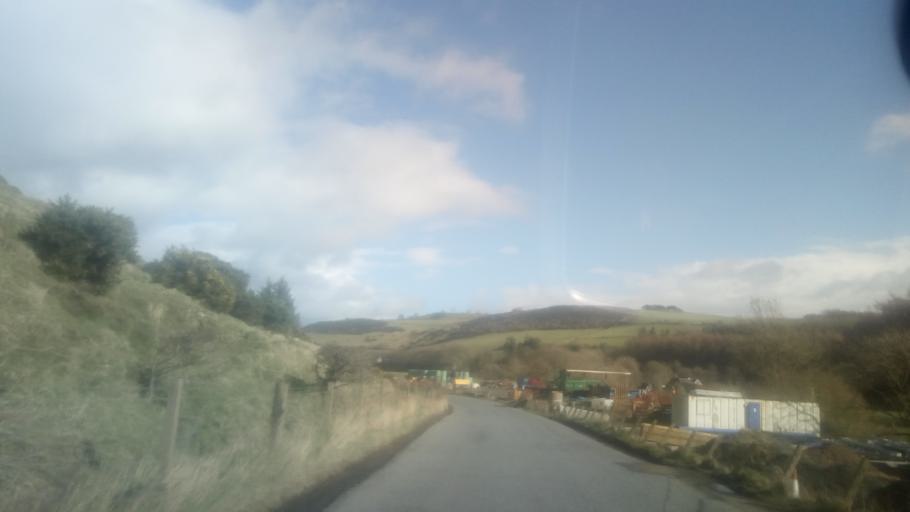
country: GB
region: Scotland
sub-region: The Scottish Borders
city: Hawick
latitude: 55.4109
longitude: -2.8348
